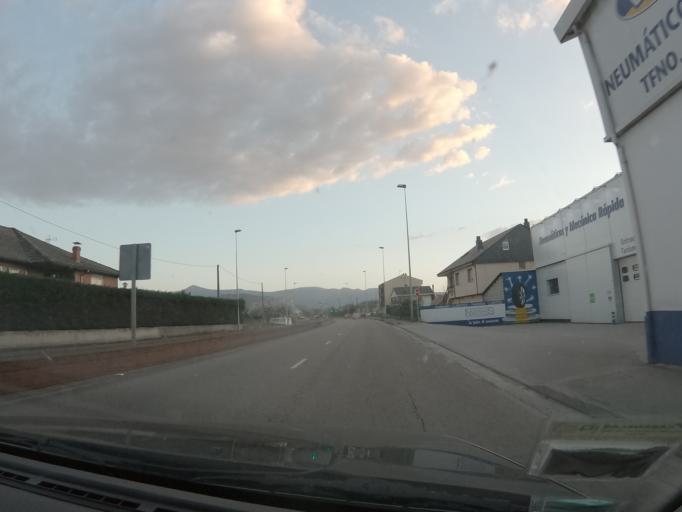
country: ES
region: Castille and Leon
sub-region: Provincia de Leon
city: Ponferrada
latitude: 42.5780
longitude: -6.6093
